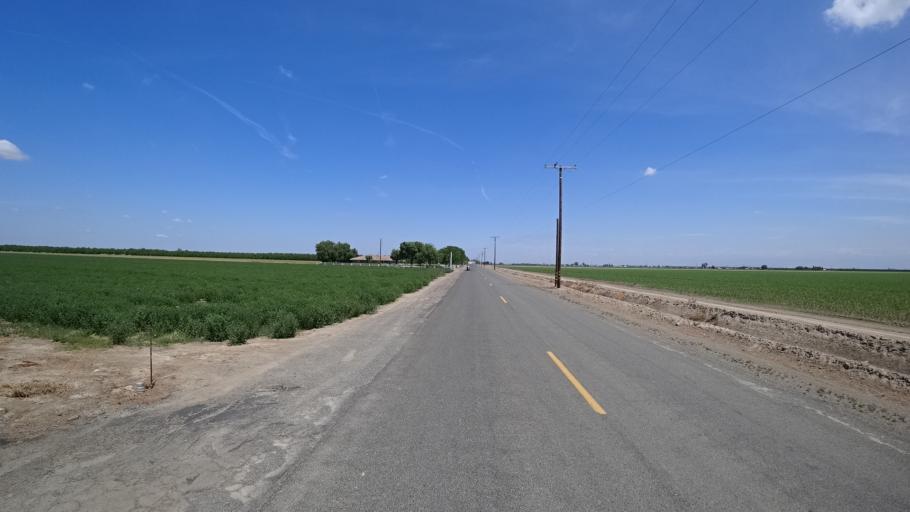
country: US
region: California
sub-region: Tulare County
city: Goshen
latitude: 36.3069
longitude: -119.4749
